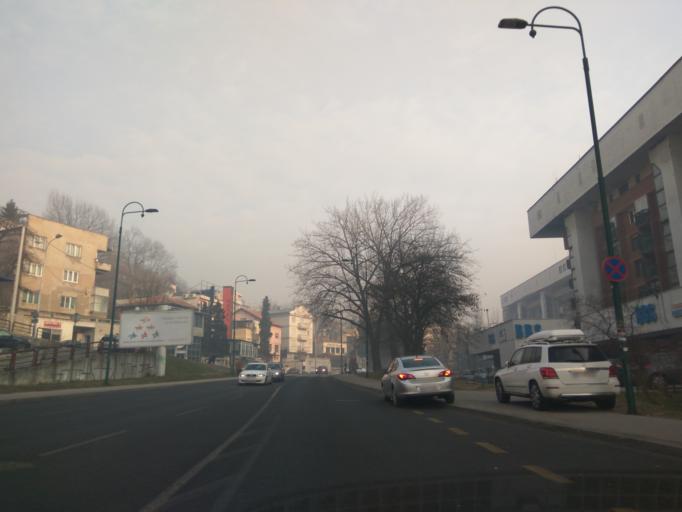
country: BA
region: Federation of Bosnia and Herzegovina
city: Kobilja Glava
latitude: 43.8589
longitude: 18.4021
